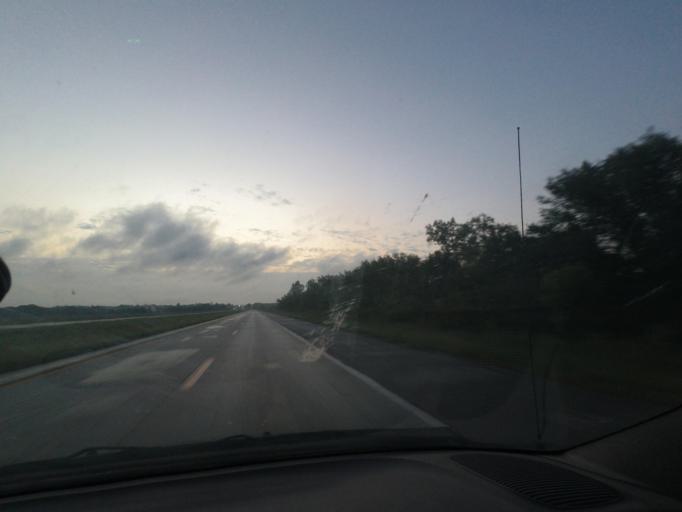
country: US
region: Missouri
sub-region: Linn County
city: Marceline
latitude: 39.7612
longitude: -92.9718
